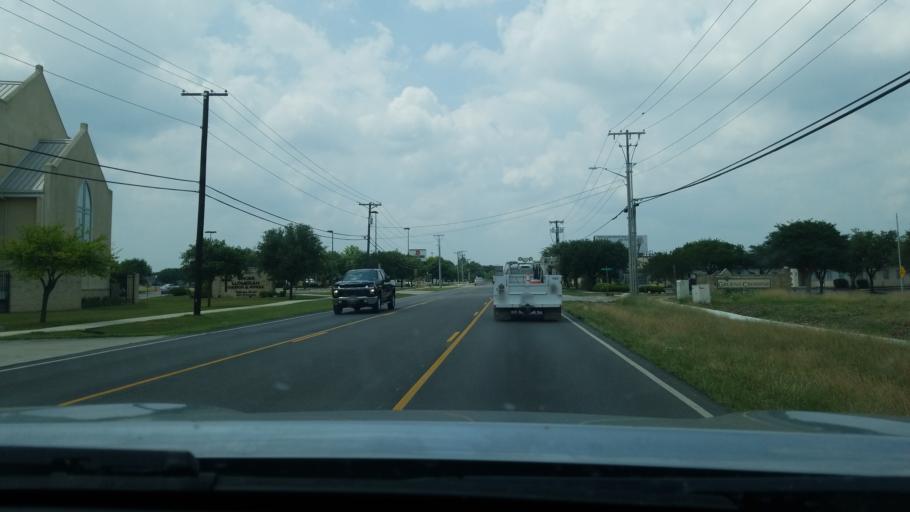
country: US
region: Texas
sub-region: Comal County
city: New Braunfels
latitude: 29.7295
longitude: -98.0959
